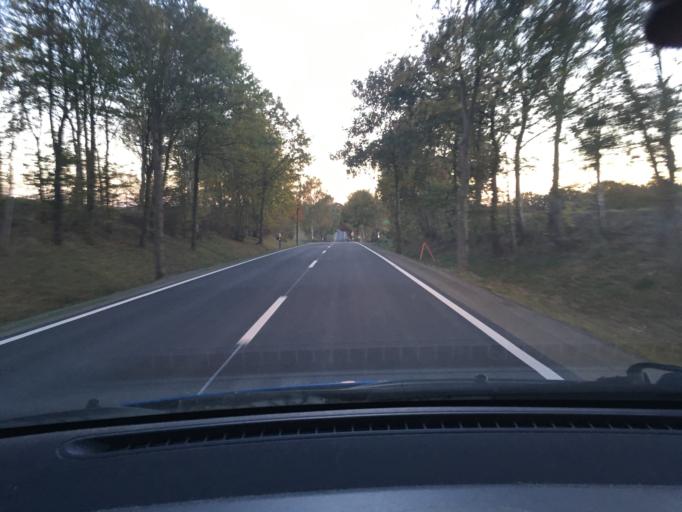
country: DE
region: Lower Saxony
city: Reinstorf
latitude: 53.2457
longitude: 10.5924
